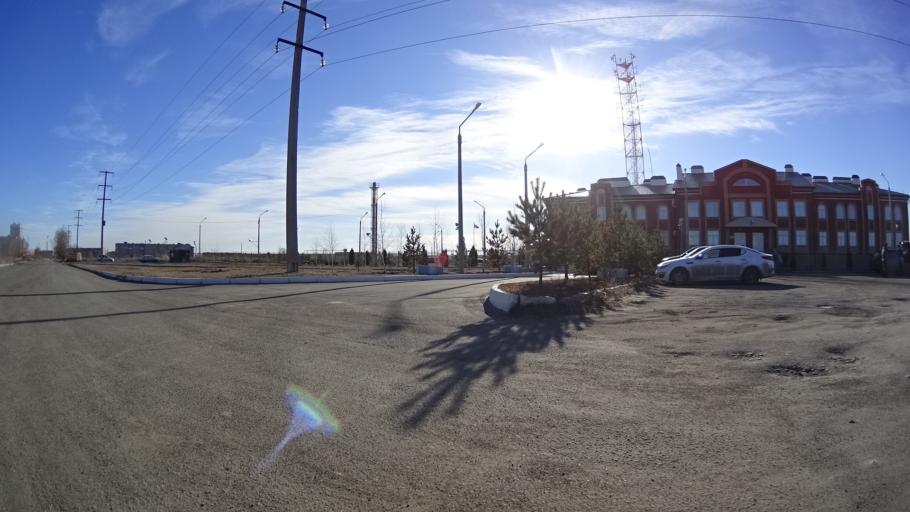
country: RU
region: Chelyabinsk
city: Troitsk
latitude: 54.0781
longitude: 61.5201
